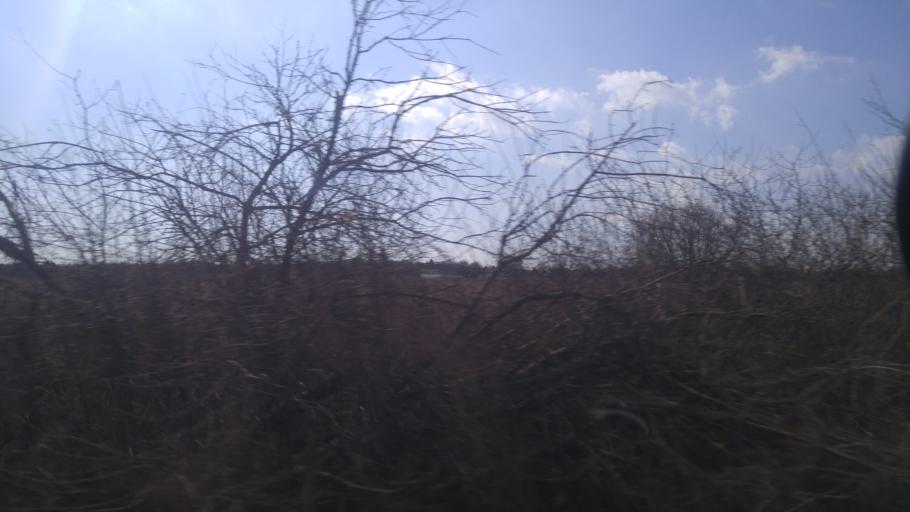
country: TR
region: Istanbul
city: Canta
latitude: 41.1694
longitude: 28.0961
